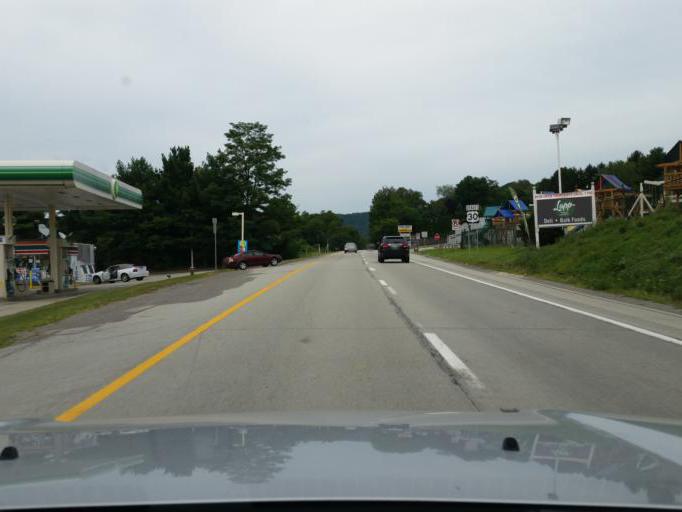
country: US
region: Pennsylvania
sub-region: Westmoreland County
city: Lawson Heights
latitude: 40.2894
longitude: -79.3585
